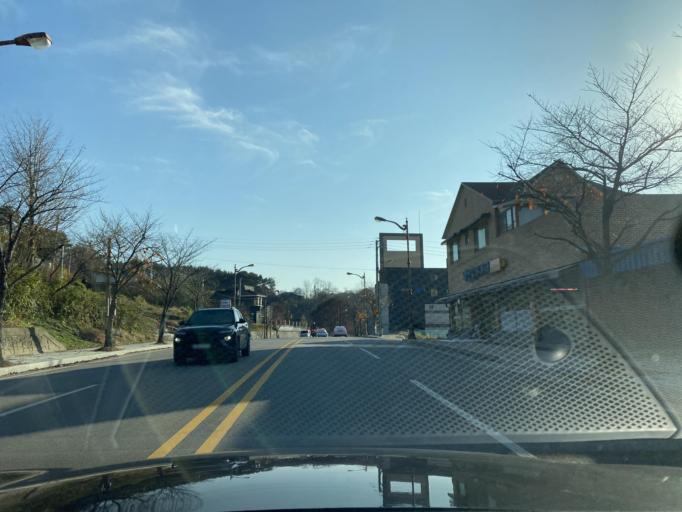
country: KR
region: Chungcheongnam-do
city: Yesan
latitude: 36.6846
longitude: 126.8359
